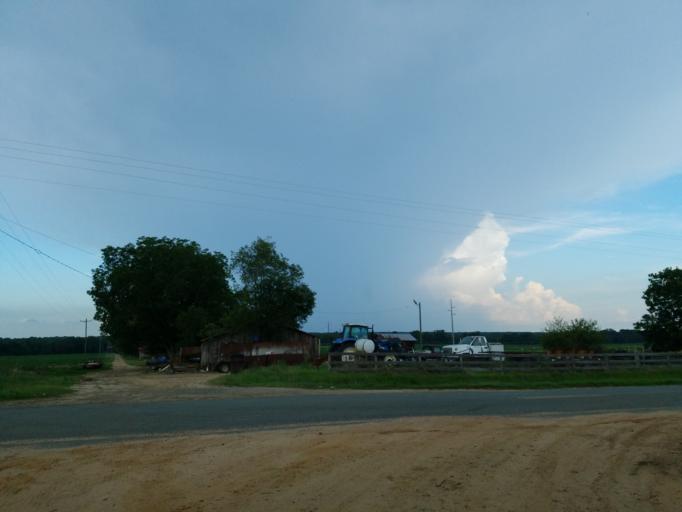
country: US
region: Georgia
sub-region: Tift County
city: Omega
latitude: 31.2742
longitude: -83.5191
